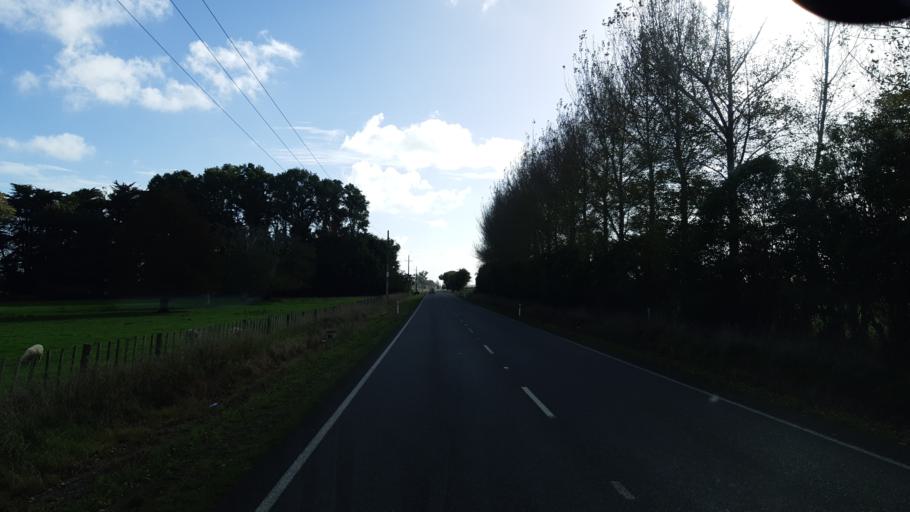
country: NZ
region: Manawatu-Wanganui
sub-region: Wanganui District
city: Wanganui
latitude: -39.9598
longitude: 175.1881
